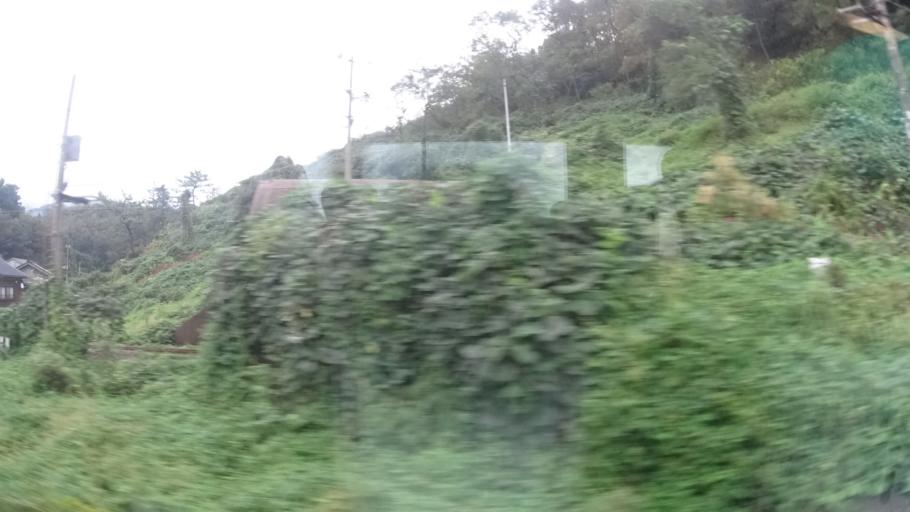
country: JP
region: Yamagata
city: Tsuruoka
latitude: 38.5889
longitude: 139.5642
